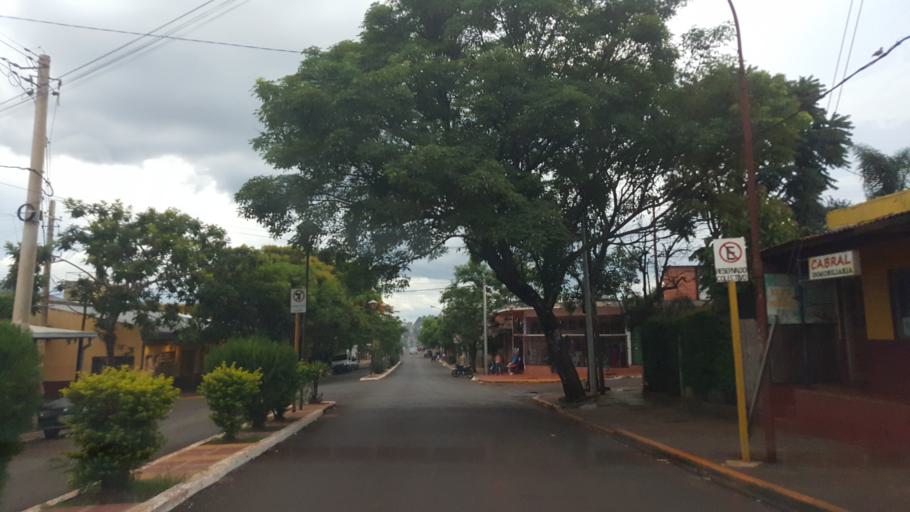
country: AR
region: Misiones
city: Jardin America
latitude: -27.0443
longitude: -55.2271
